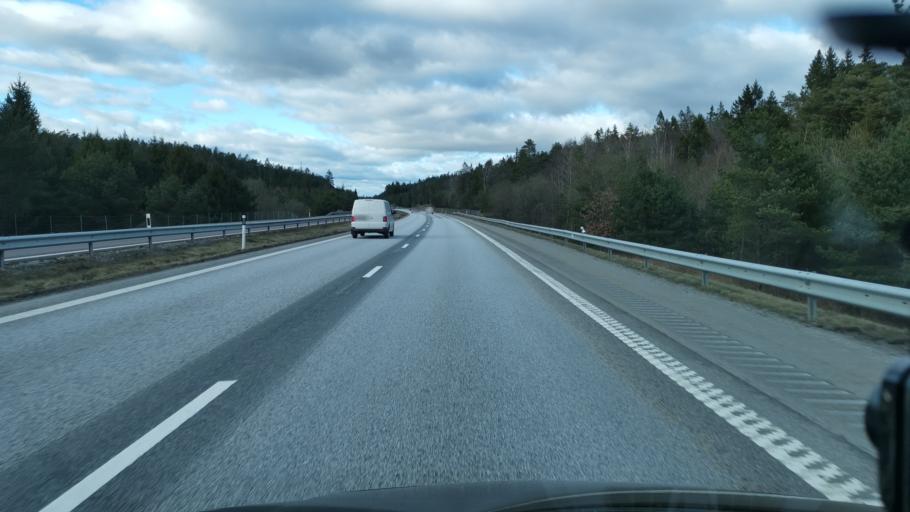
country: SE
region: Vaestra Goetaland
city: Svanesund
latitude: 58.1321
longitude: 11.8860
